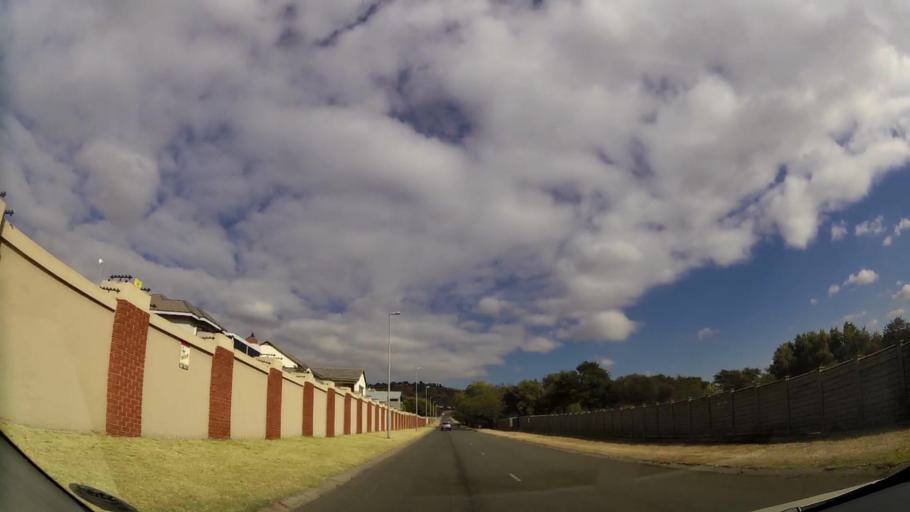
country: ZA
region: Gauteng
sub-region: City of Johannesburg Metropolitan Municipality
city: Roodepoort
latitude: -26.1027
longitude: 27.8771
